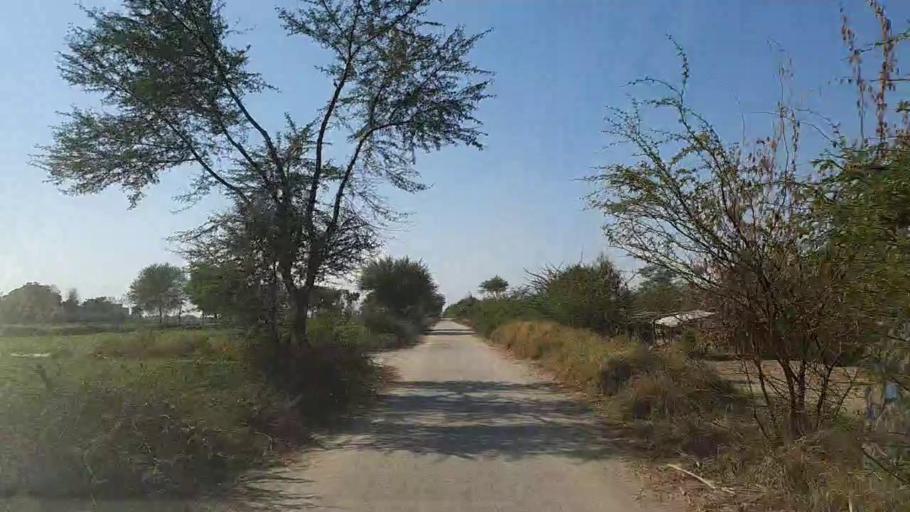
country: PK
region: Sindh
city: Nawabshah
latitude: 26.2449
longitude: 68.4420
